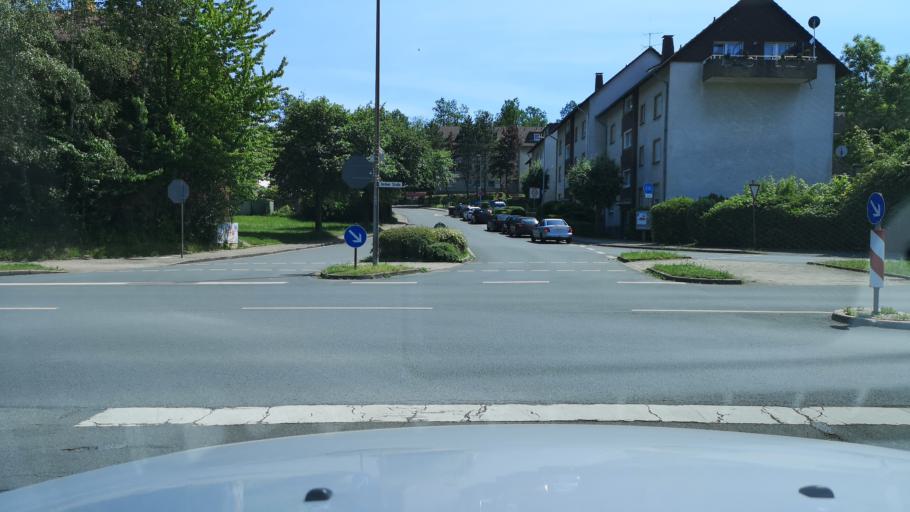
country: DE
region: North Rhine-Westphalia
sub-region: Regierungsbezirk Arnsberg
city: Menden
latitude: 51.4350
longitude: 7.7806
